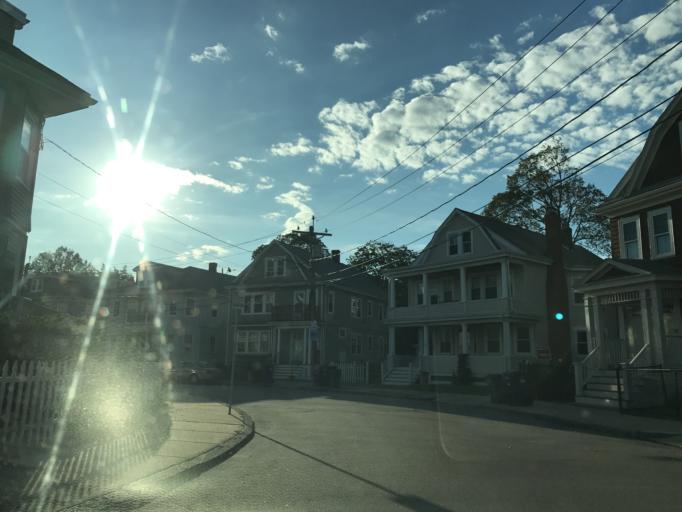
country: US
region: Massachusetts
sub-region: Norfolk County
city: Milton
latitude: 42.2917
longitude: -71.0593
